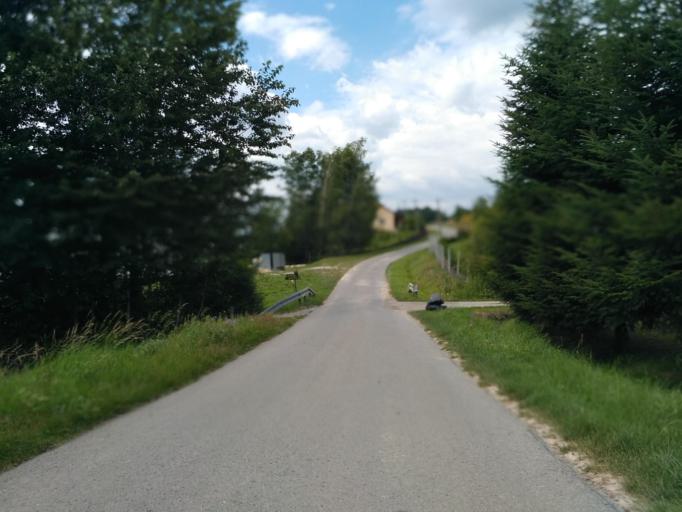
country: PL
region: Subcarpathian Voivodeship
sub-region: Powiat rzeszowski
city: Chmielnik
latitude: 49.9533
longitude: 22.1231
